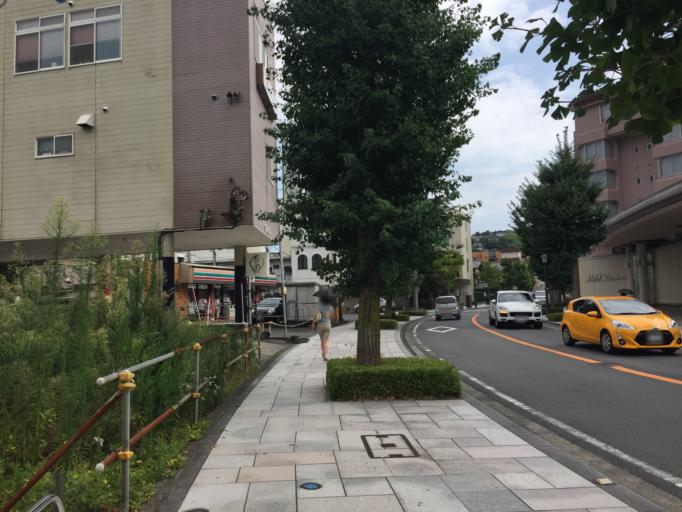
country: JP
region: Shizuoka
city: Ito
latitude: 34.9694
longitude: 139.0975
